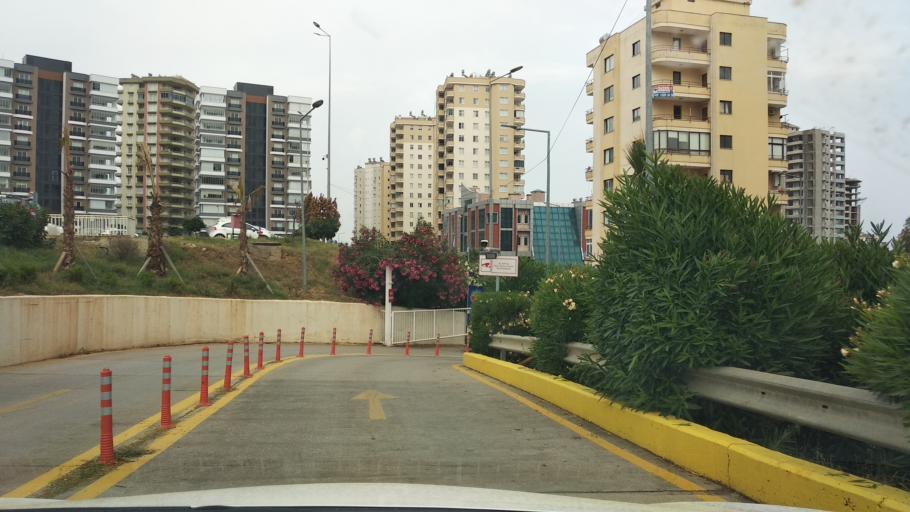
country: TR
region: Mersin
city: Mercin
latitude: 36.7993
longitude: 34.5956
